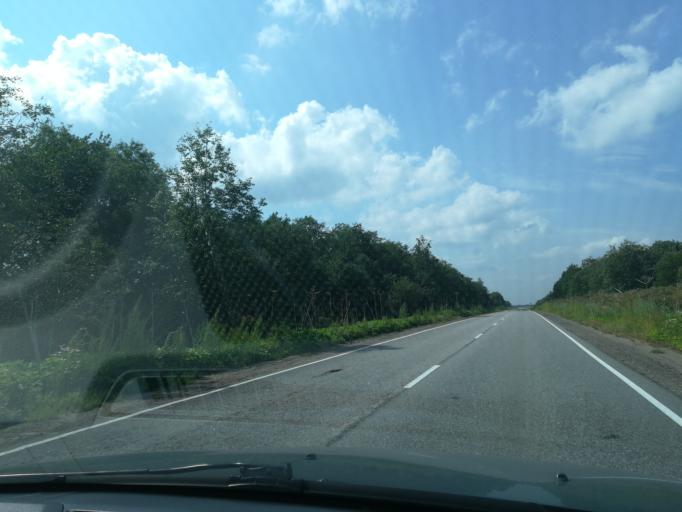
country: RU
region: Leningrad
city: Kopor'ye
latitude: 59.6891
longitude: 29.0479
